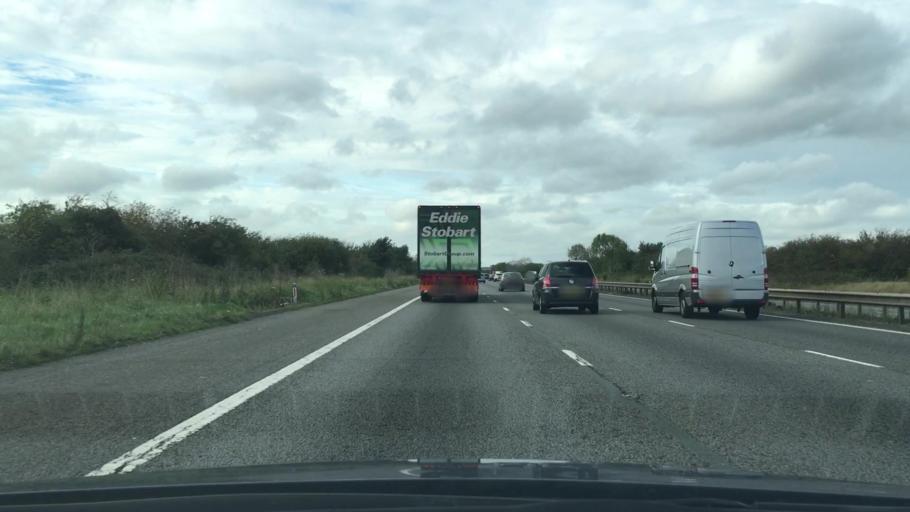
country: GB
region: England
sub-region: Milton Keynes
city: Hanslope
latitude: 52.1195
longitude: -0.8053
